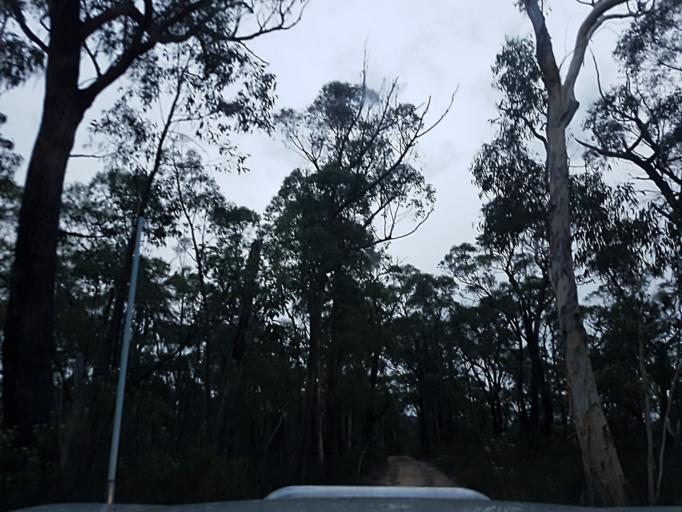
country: AU
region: New South Wales
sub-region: Snowy River
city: Jindabyne
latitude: -36.8622
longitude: 148.2360
